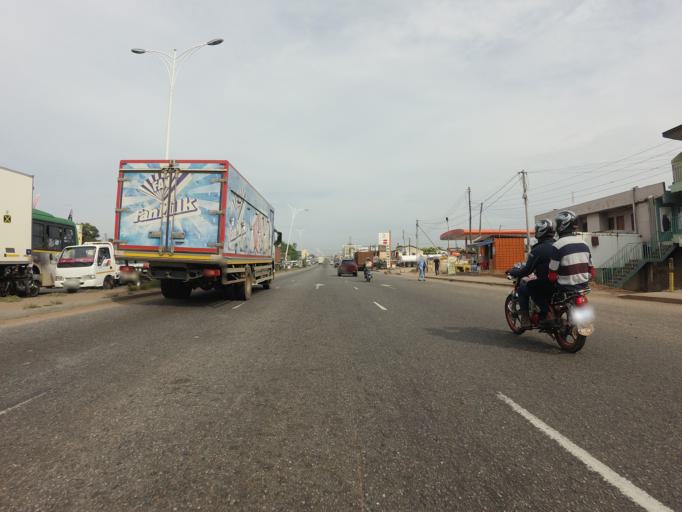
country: GH
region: Greater Accra
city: Dome
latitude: 5.6209
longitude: -0.2309
